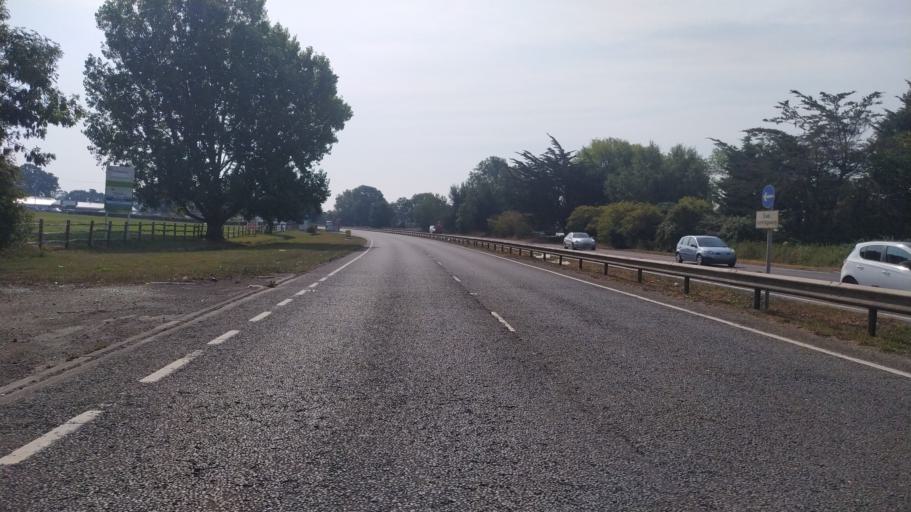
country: GB
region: England
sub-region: West Sussex
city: Chichester
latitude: 50.8280
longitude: -0.7412
